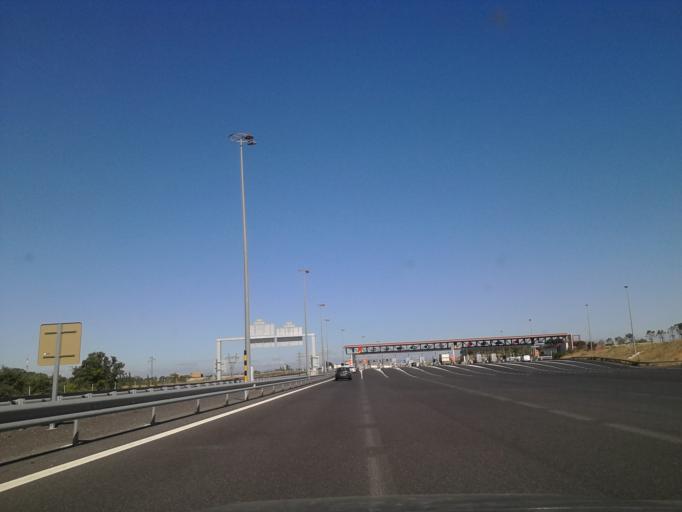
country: FR
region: Languedoc-Roussillon
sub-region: Departement de l'Herault
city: Cers
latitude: 43.3419
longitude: 3.2918
